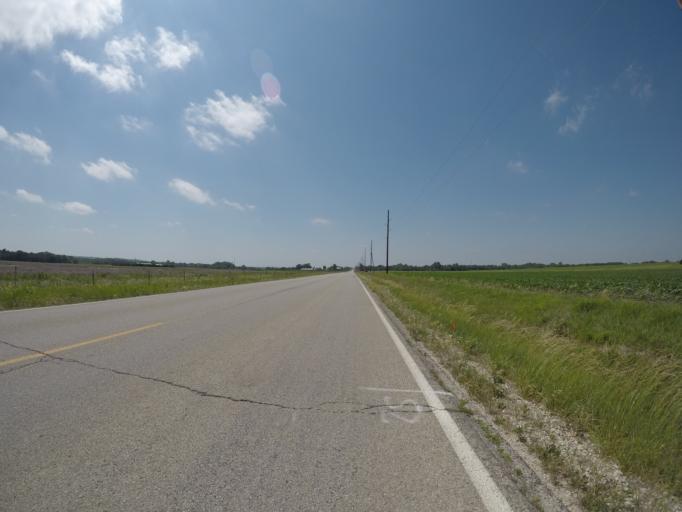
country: US
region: Kansas
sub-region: Pottawatomie County
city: Westmoreland
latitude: 39.3358
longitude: -96.4361
